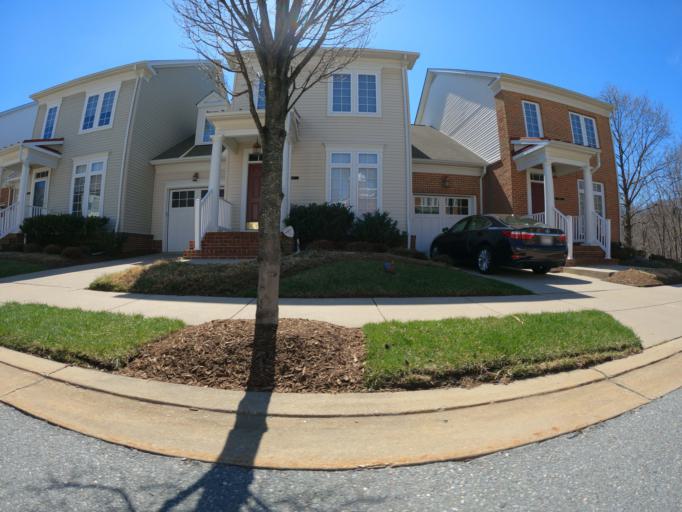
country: US
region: Maryland
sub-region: Howard County
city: Ellicott City
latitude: 39.2935
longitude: -76.8194
